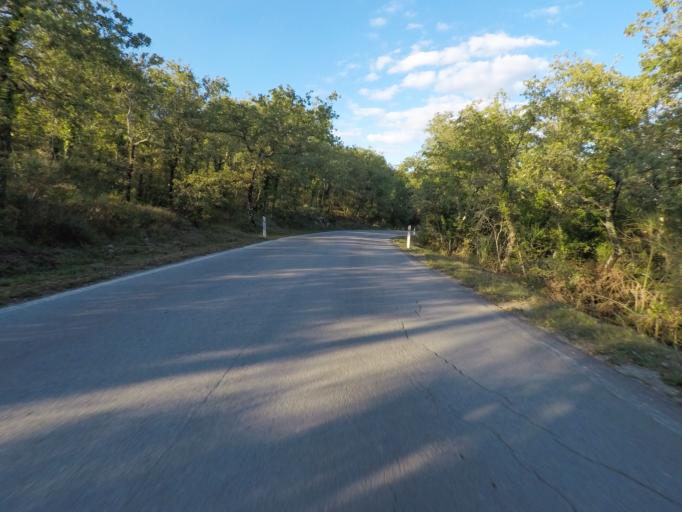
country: IT
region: Tuscany
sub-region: Provincia di Siena
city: Radda in Chianti
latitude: 43.4561
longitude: 11.3839
